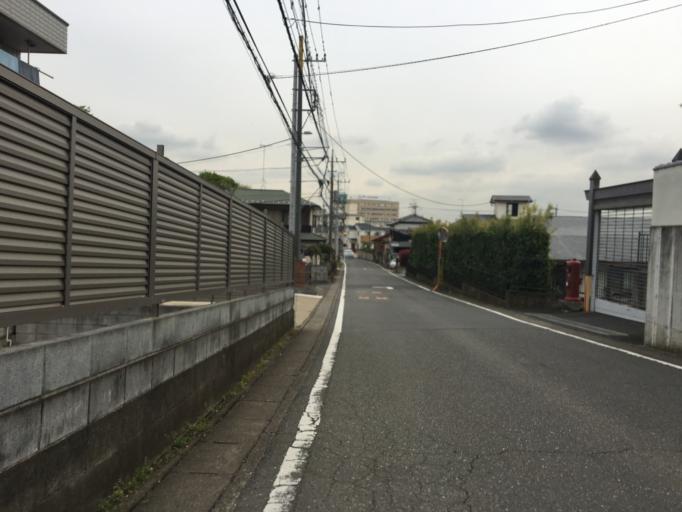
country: JP
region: Saitama
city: Oi
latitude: 35.8537
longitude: 139.5489
